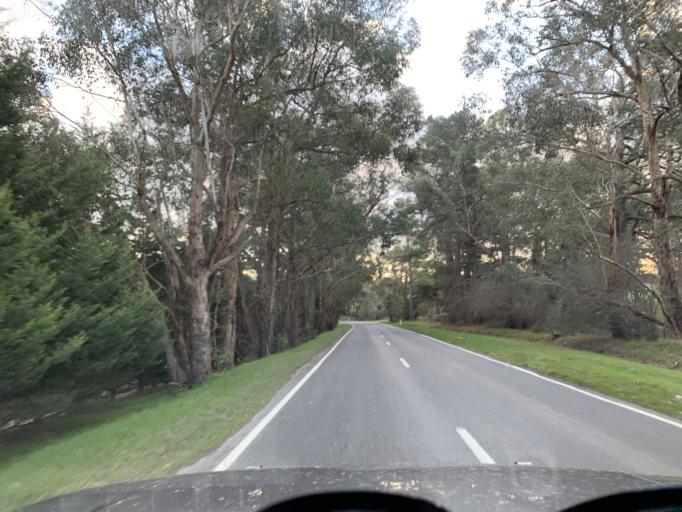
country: AU
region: Victoria
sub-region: Yarra Ranges
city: Woori Yallock
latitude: -37.7848
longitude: 145.5276
